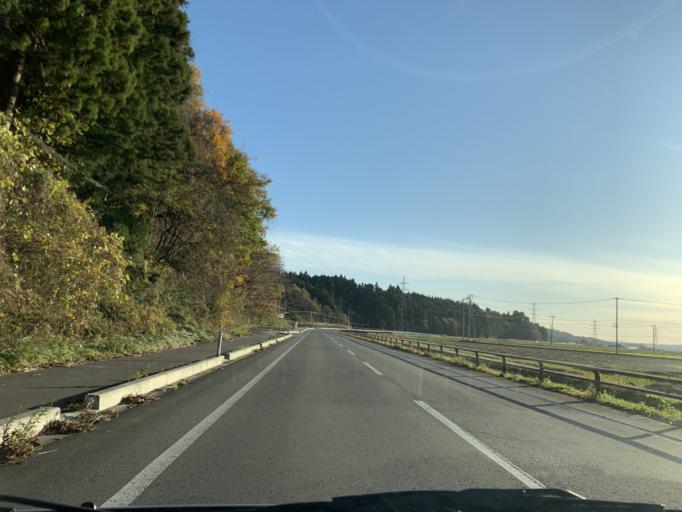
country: JP
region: Iwate
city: Mizusawa
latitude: 39.0772
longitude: 141.1897
